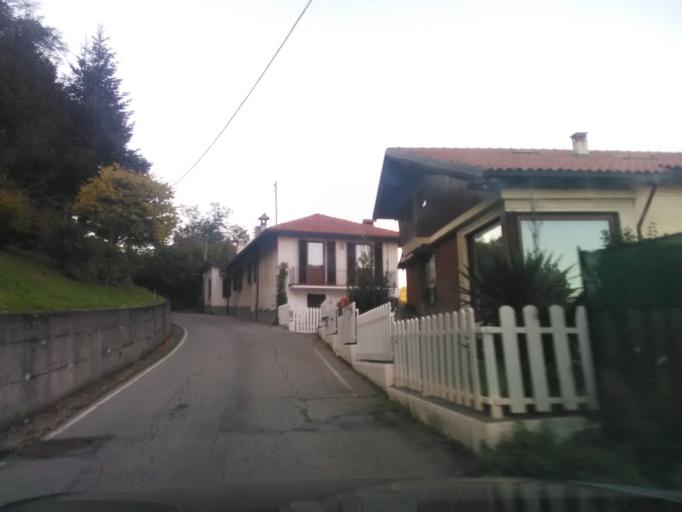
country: IT
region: Piedmont
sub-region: Provincia di Vercelli
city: Borgosesia
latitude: 45.7210
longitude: 8.2807
